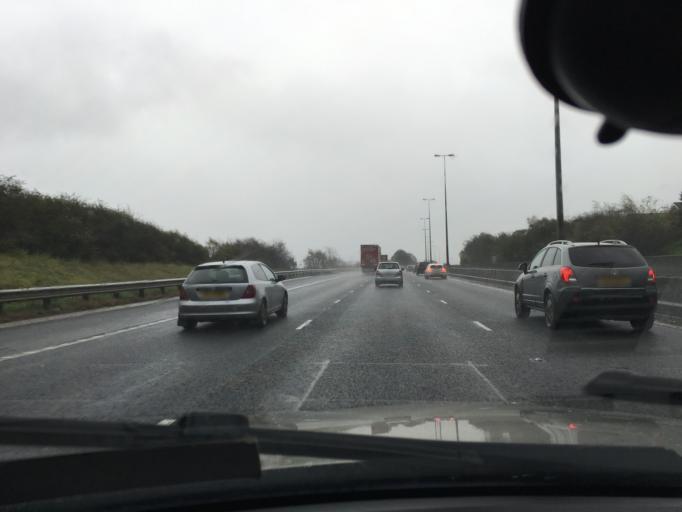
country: GB
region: Northern Ireland
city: Carnmoney
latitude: 54.6689
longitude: -5.9616
